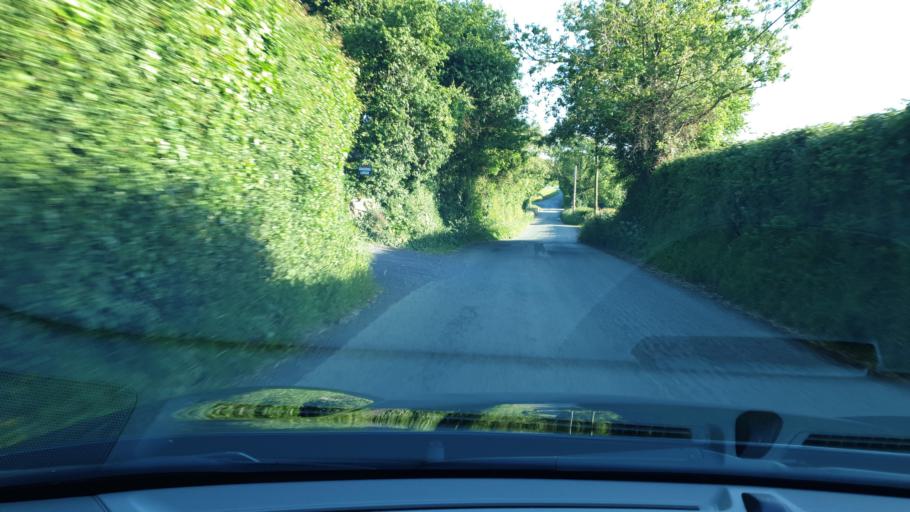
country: IE
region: Leinster
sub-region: Fingal County
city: Swords
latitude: 53.5107
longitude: -6.2354
